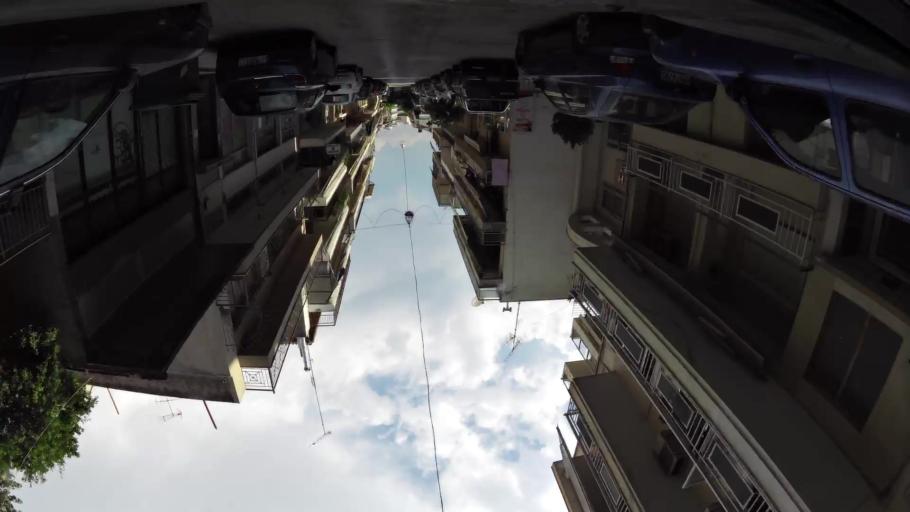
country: GR
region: Central Macedonia
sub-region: Nomos Thessalonikis
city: Polichni
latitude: 40.6601
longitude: 22.9484
